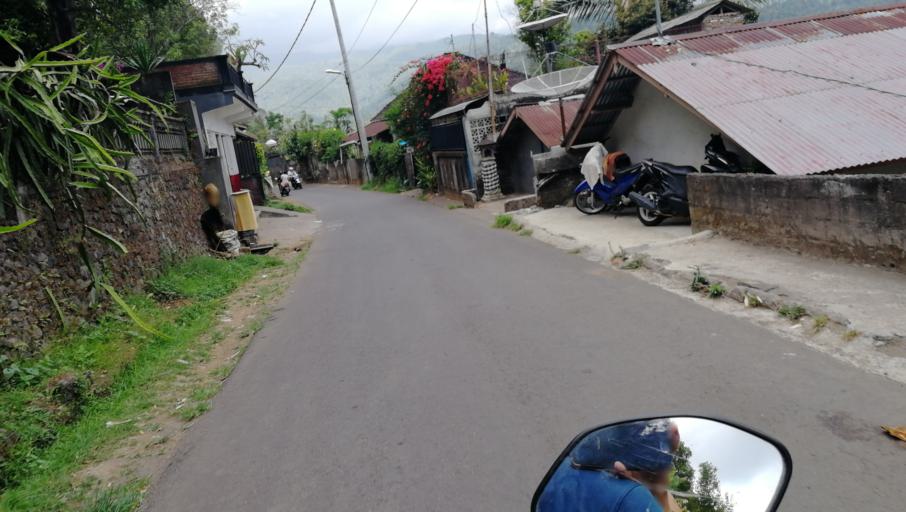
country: ID
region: Bali
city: Banjar Pedawa
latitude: -8.2648
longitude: 115.0426
